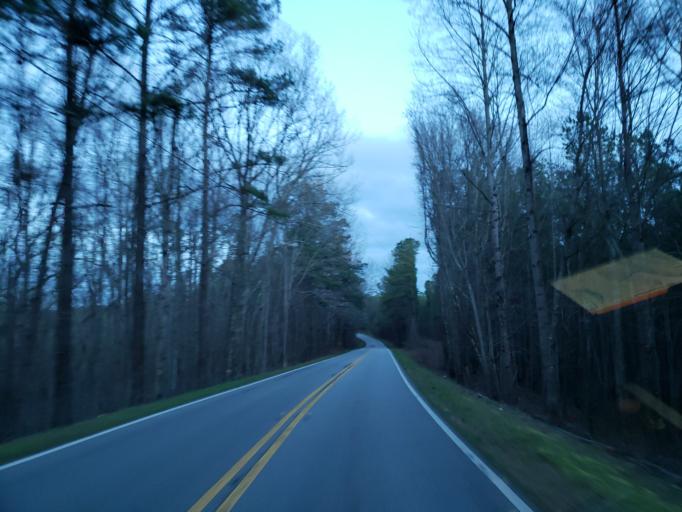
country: US
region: Georgia
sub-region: Paulding County
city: Dallas
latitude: 34.0028
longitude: -84.9203
